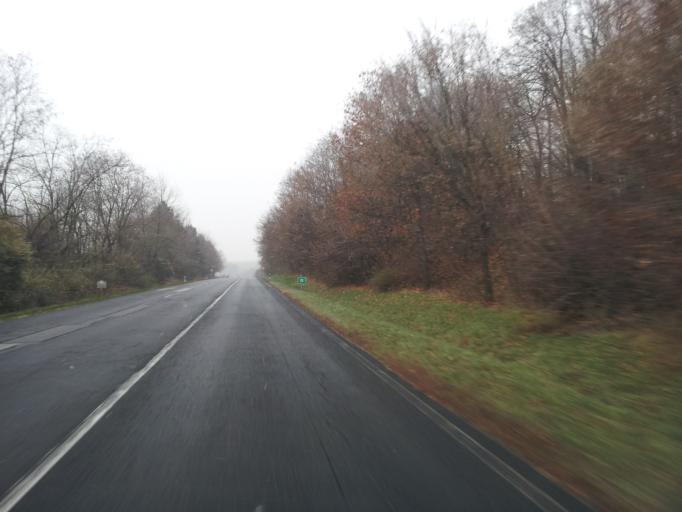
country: HU
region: Veszprem
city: Urkut
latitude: 47.1523
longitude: 17.6369
